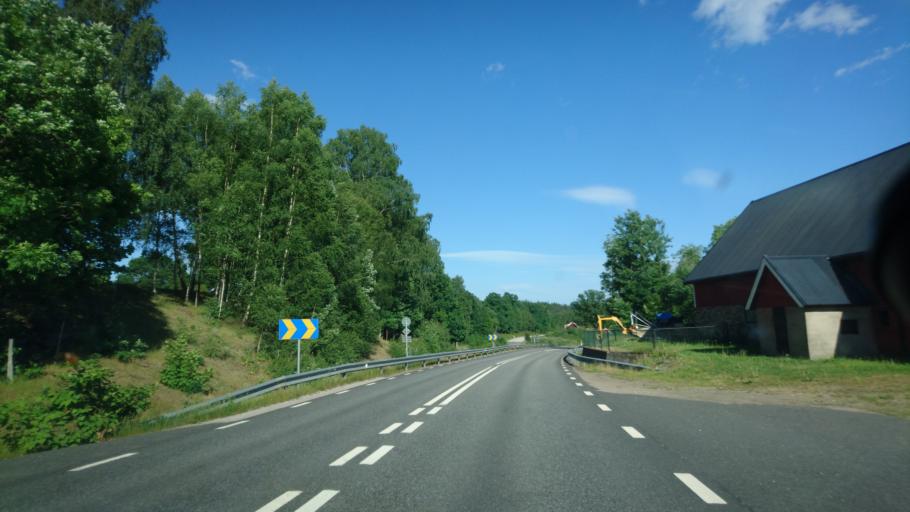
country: SE
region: Skane
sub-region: Osby Kommun
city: Lonsboda
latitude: 56.3911
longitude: 14.4534
